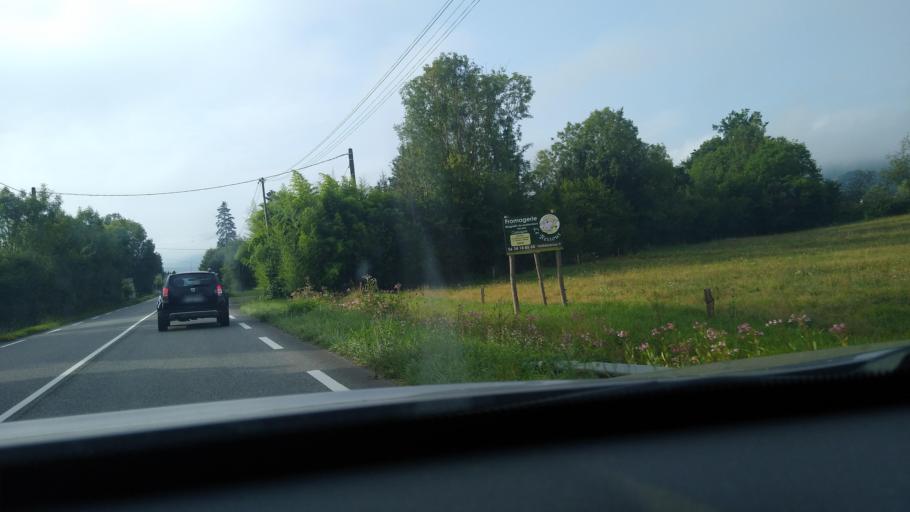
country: FR
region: Midi-Pyrenees
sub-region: Departement de la Haute-Garonne
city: Salies-du-Salat
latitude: 43.0575
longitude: 0.9771
